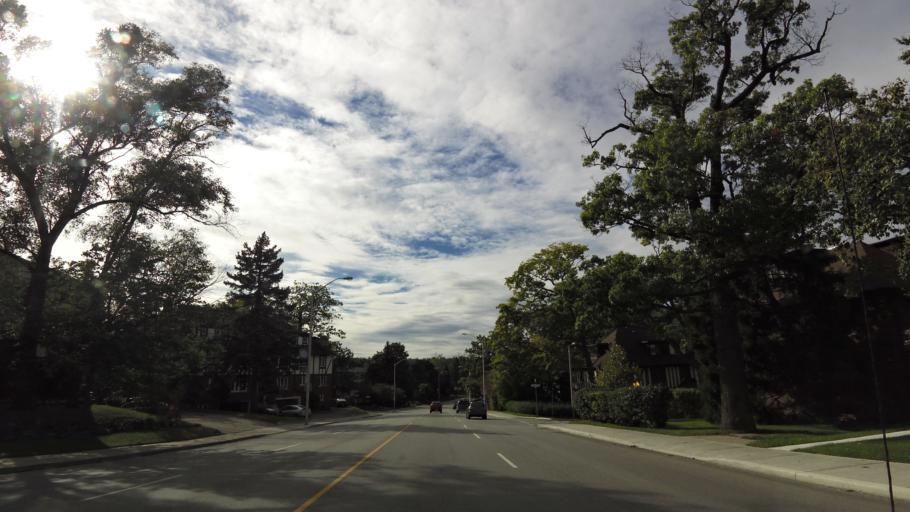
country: CA
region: Ontario
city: Etobicoke
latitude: 43.6477
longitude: -79.4881
